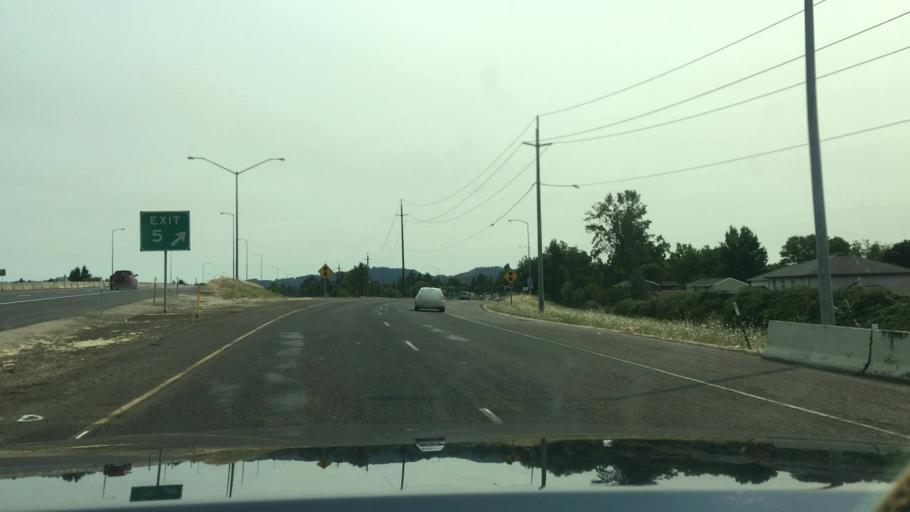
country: US
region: Oregon
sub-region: Lane County
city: Eugene
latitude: 44.0874
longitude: -123.1719
